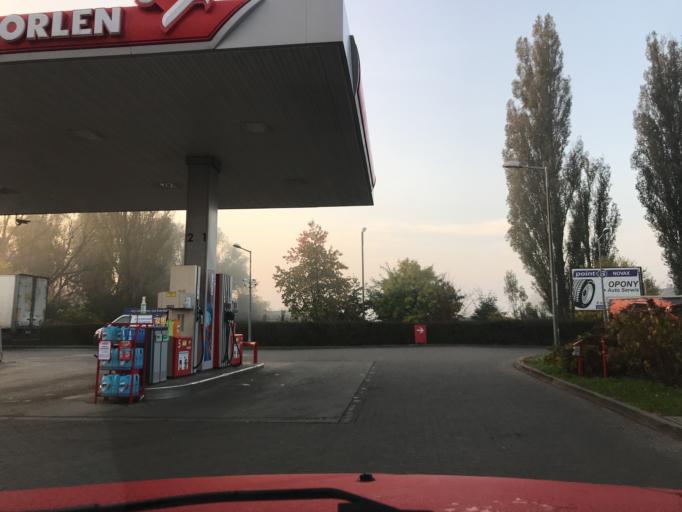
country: PL
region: Greater Poland Voivodeship
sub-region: Powiat poznanski
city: Baranowo
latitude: 52.4311
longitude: 16.8087
